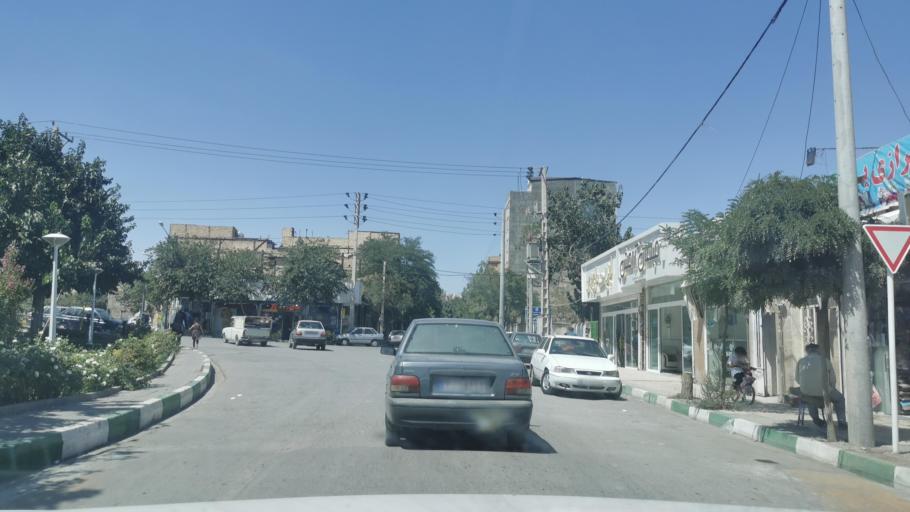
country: IR
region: Razavi Khorasan
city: Mashhad
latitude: 36.3612
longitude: 59.5585
